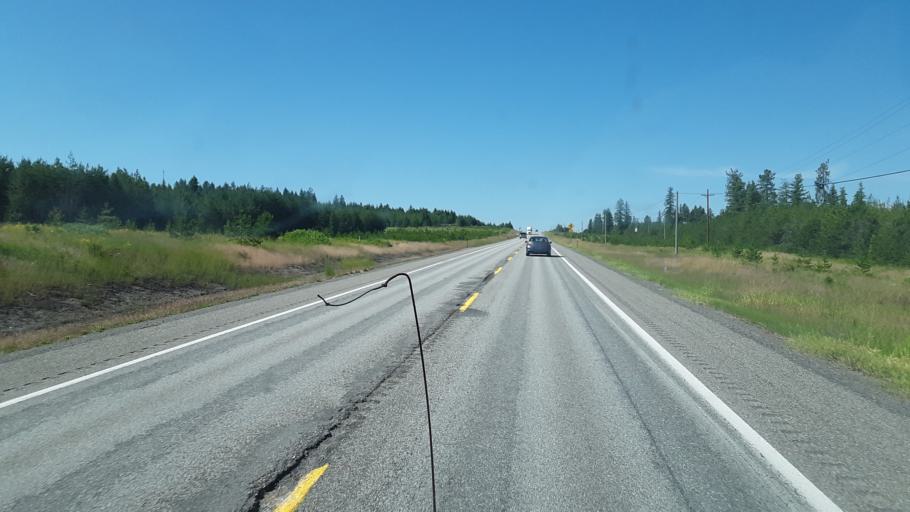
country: US
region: Idaho
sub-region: Kootenai County
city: Spirit Lake
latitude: 48.0126
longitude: -116.6613
